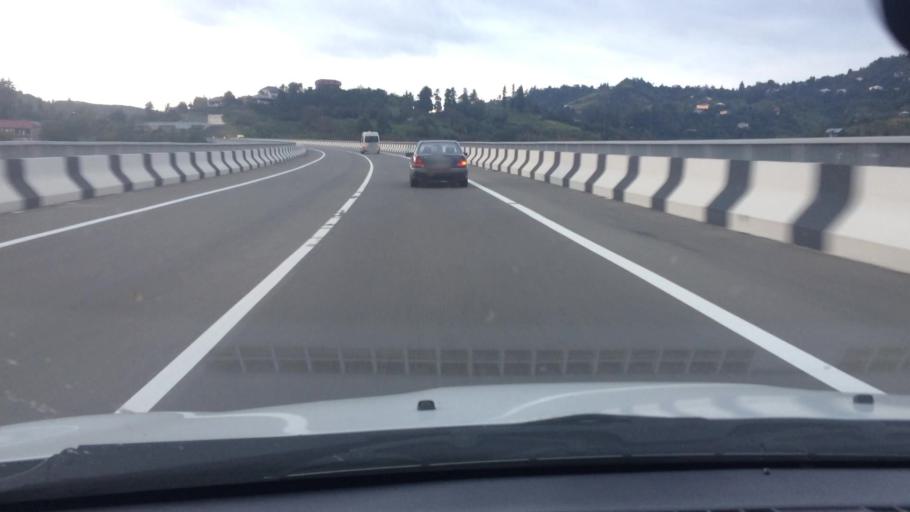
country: GE
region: Ajaria
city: Makhinjauri
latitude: 41.7144
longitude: 41.7518
